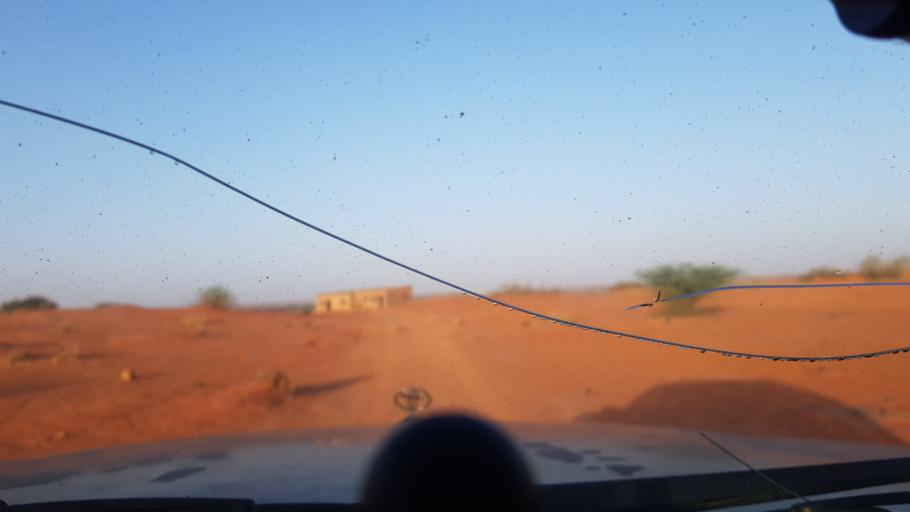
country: NE
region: Niamey
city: Niamey
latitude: 13.5169
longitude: 2.2194
